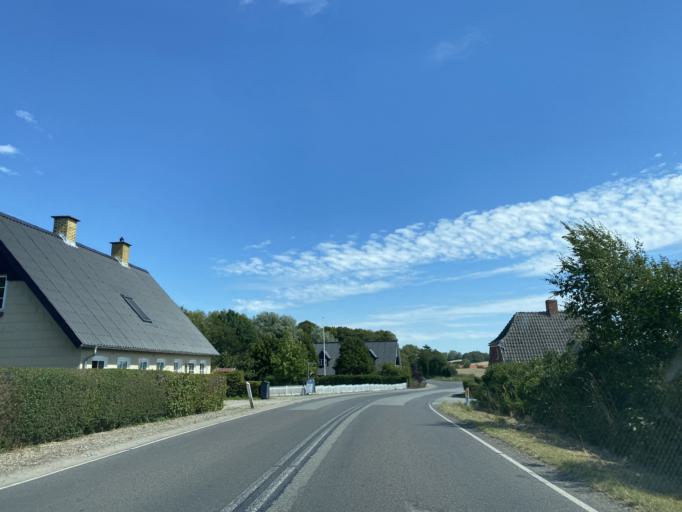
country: DK
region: South Denmark
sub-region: Faaborg-Midtfyn Kommune
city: Ringe
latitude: 55.2105
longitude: 10.3684
